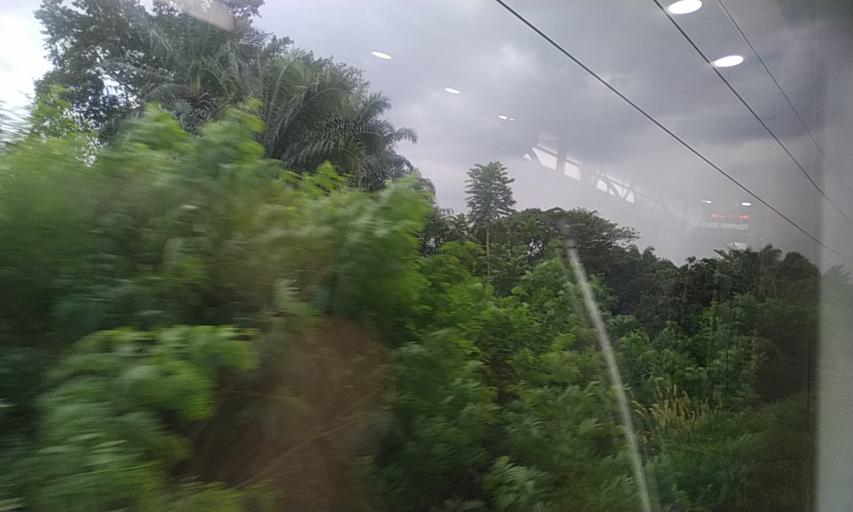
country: MY
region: Kuala Lumpur
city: Kuala Lumpur
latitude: 3.2313
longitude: 101.6755
